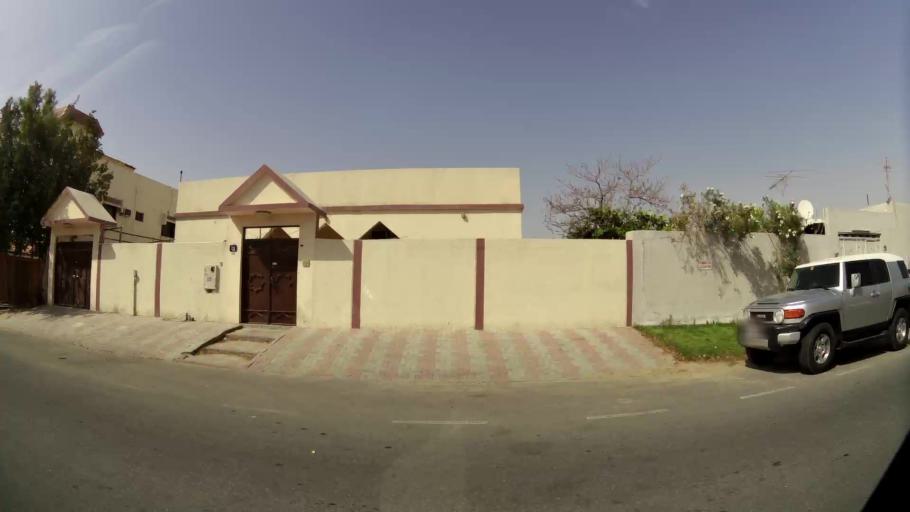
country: AE
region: Dubai
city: Dubai
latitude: 25.1692
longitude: 55.2478
